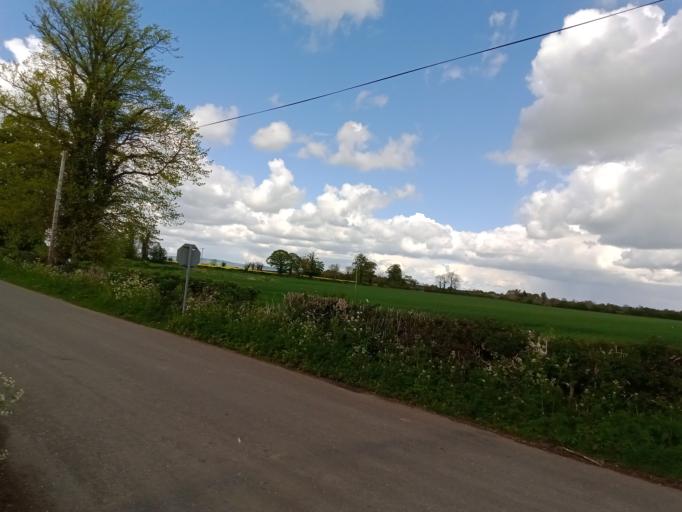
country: IE
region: Leinster
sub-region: Kilkenny
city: Thomastown
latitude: 52.5789
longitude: -7.1277
